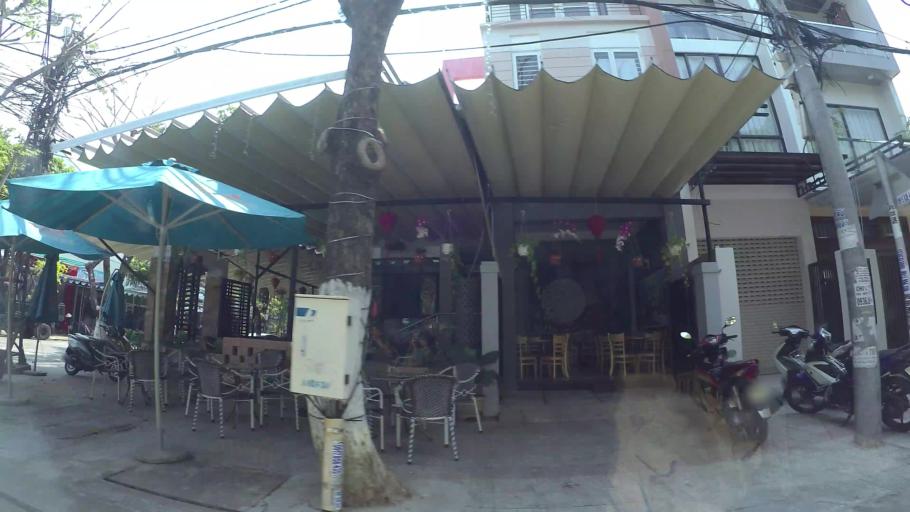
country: VN
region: Da Nang
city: Cam Le
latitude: 16.0156
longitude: 108.2064
